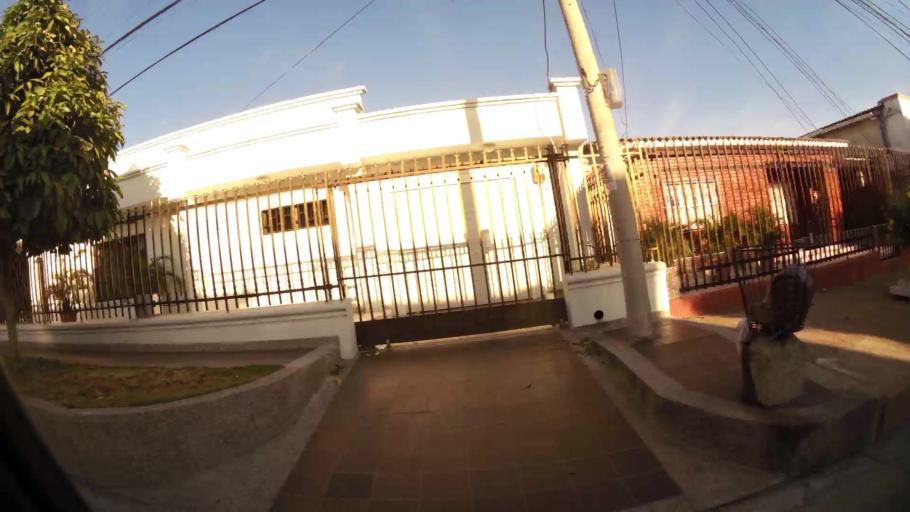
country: CO
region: Atlantico
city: Barranquilla
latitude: 10.9830
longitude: -74.8065
